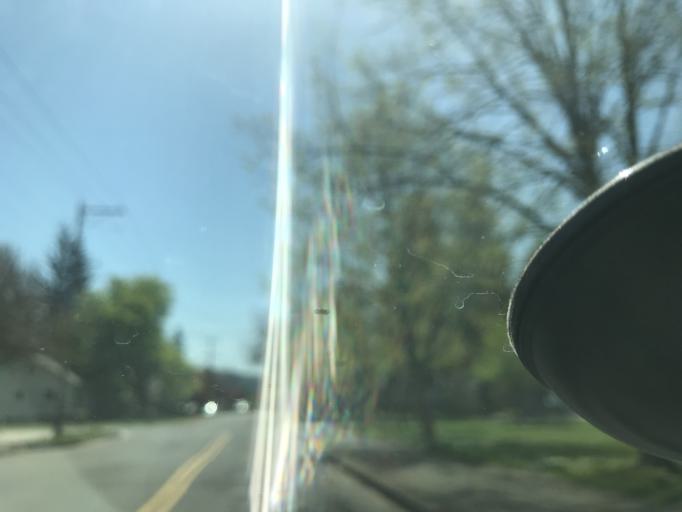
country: US
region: Oregon
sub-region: Multnomah County
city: Lents
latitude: 45.4953
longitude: -122.5560
